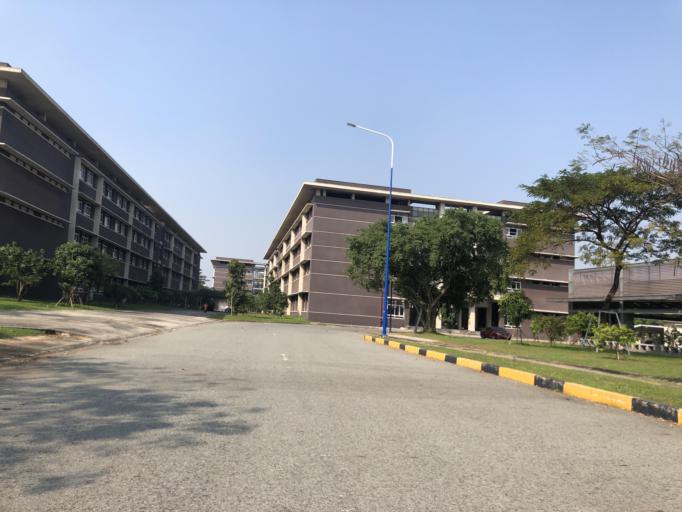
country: VN
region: Binh Duong
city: Thu Dau Mot
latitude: 11.0547
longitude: 106.6676
